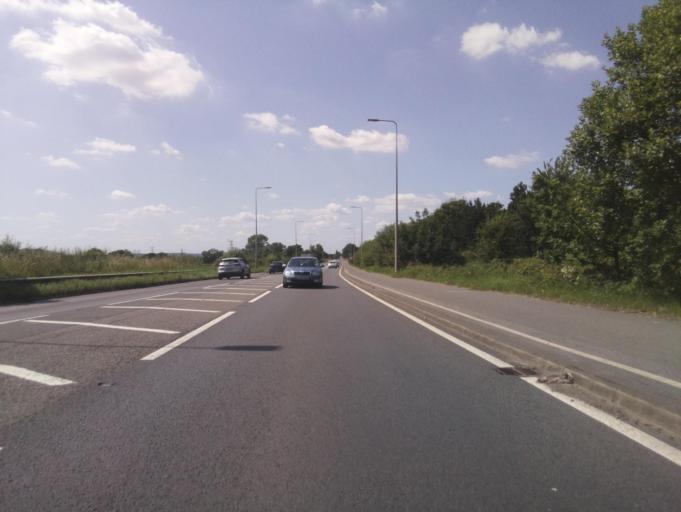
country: GB
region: England
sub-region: Leicestershire
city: Hinckley
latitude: 52.5257
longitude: -1.3894
